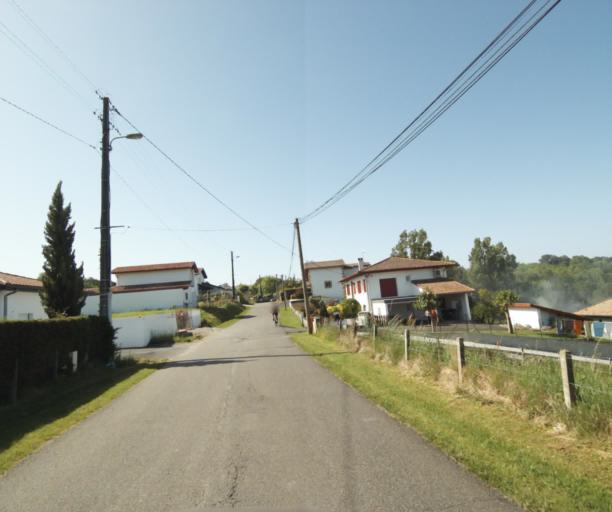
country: FR
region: Aquitaine
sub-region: Departement des Pyrenees-Atlantiques
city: Villefranque
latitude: 43.4609
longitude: -1.4487
